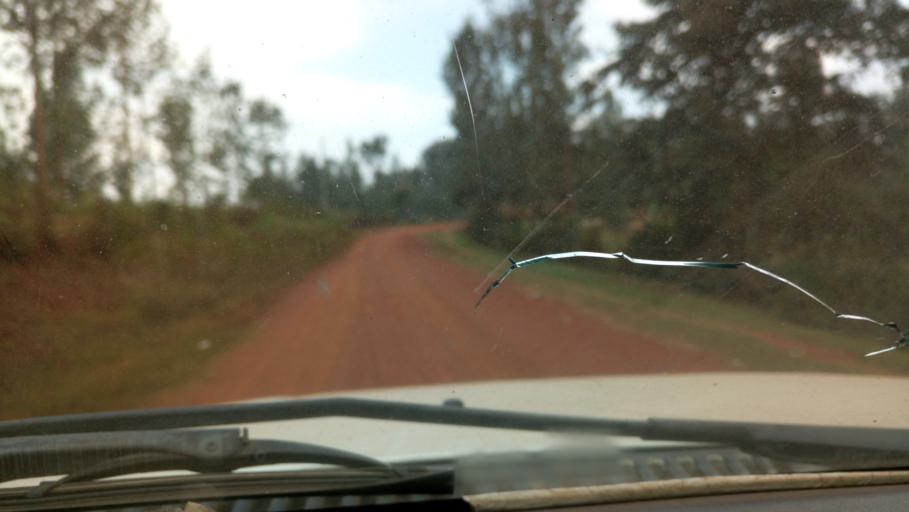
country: KE
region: Murang'a District
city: Maragua
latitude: -0.8398
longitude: 37.0197
